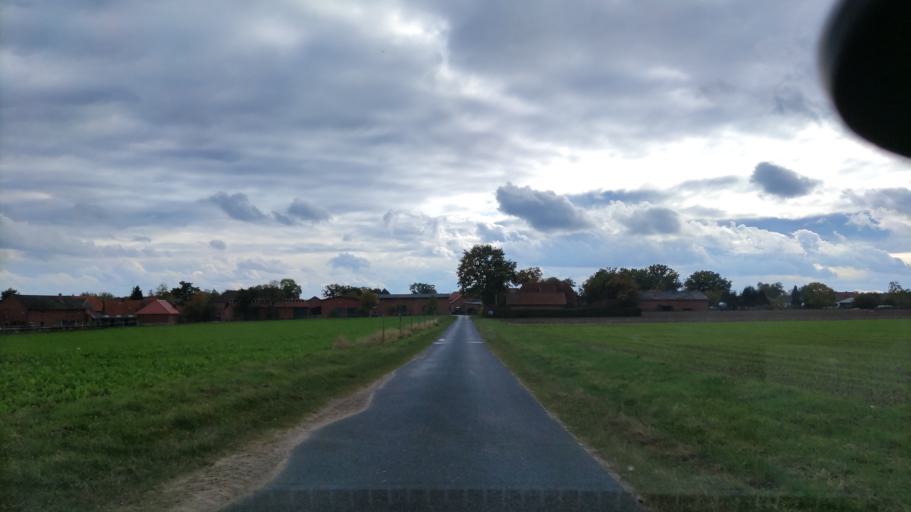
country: DE
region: Lower Saxony
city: Jelmstorf
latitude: 53.1477
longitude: 10.5344
